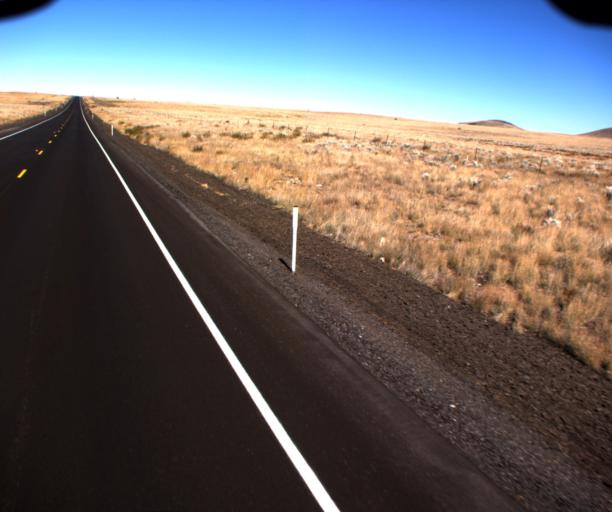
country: US
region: Arizona
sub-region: Apache County
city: Springerville
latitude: 34.2118
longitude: -109.3311
